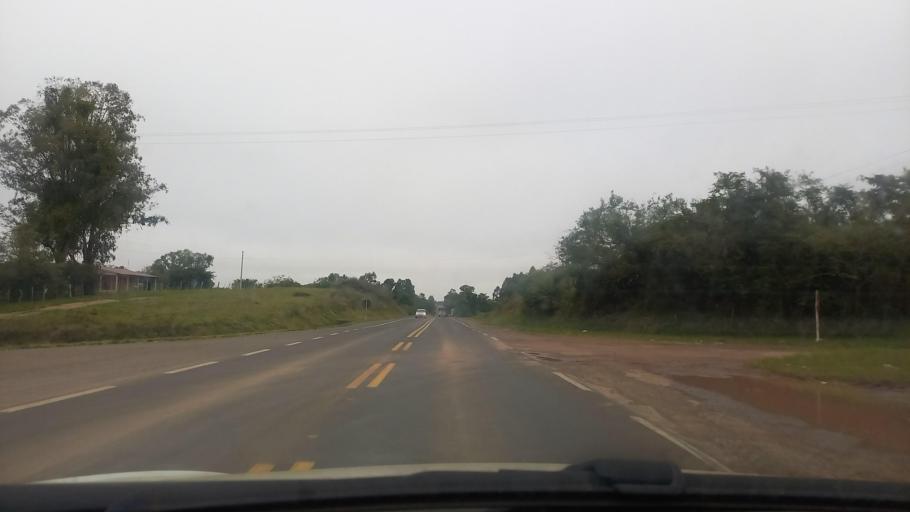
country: BR
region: Rio Grande do Sul
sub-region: Rosario Do Sul
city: Rosario do Sul
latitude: -30.2569
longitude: -54.9639
